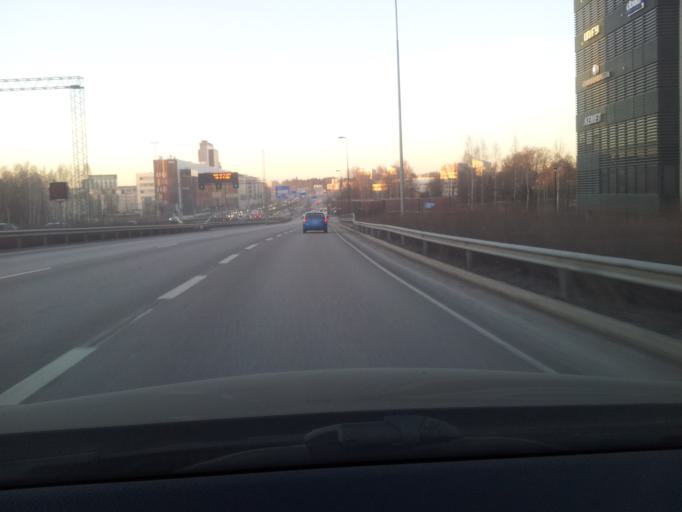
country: FI
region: Uusimaa
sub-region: Helsinki
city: Teekkarikylae
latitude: 60.2119
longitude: 24.8167
